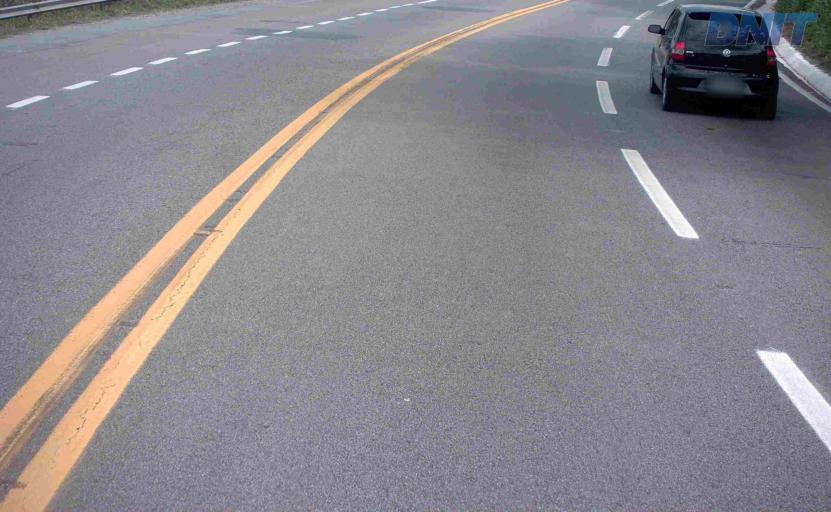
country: BR
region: Minas Gerais
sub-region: Santa Luzia
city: Santa Luzia
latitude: -19.8000
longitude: -43.7496
